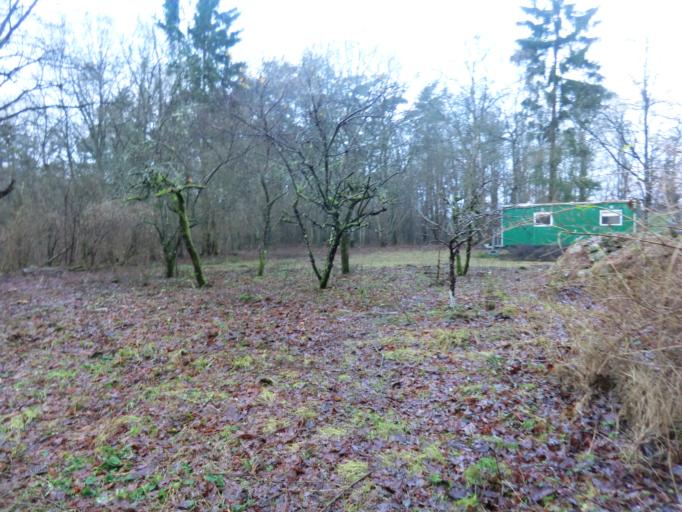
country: SE
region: Skane
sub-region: Hoors Kommun
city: Loberod
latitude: 55.7298
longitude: 13.4009
